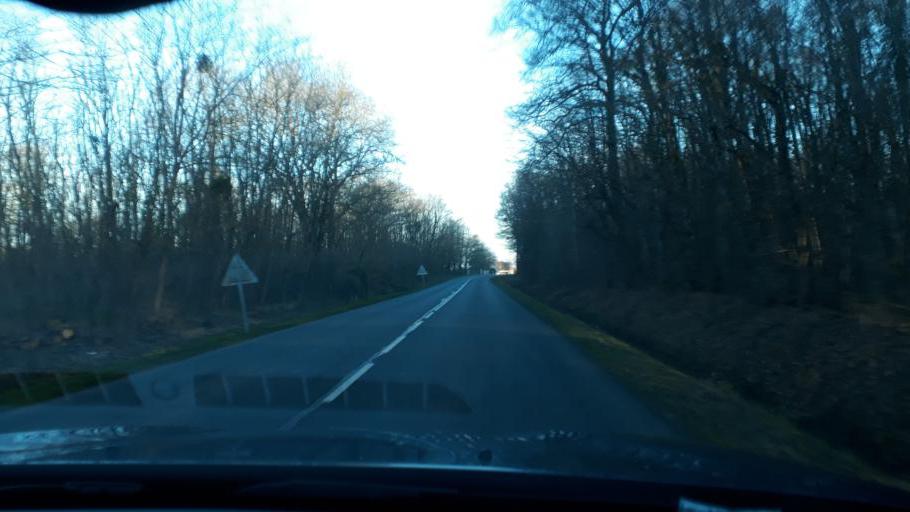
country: FR
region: Centre
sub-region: Departement du Loiret
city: Neuville-aux-Bois
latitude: 48.0441
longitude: 2.0500
